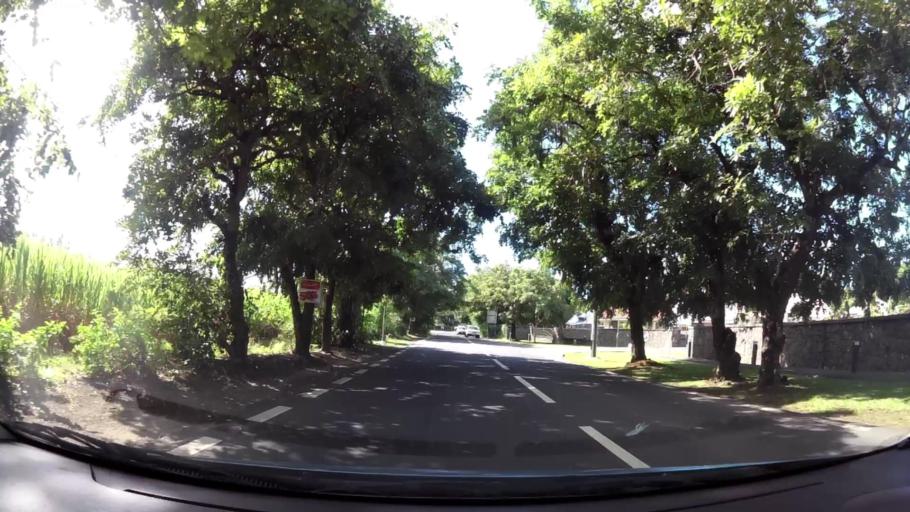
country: MU
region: Grand Port
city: Beau Vallon
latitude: -20.4239
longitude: 57.6999
